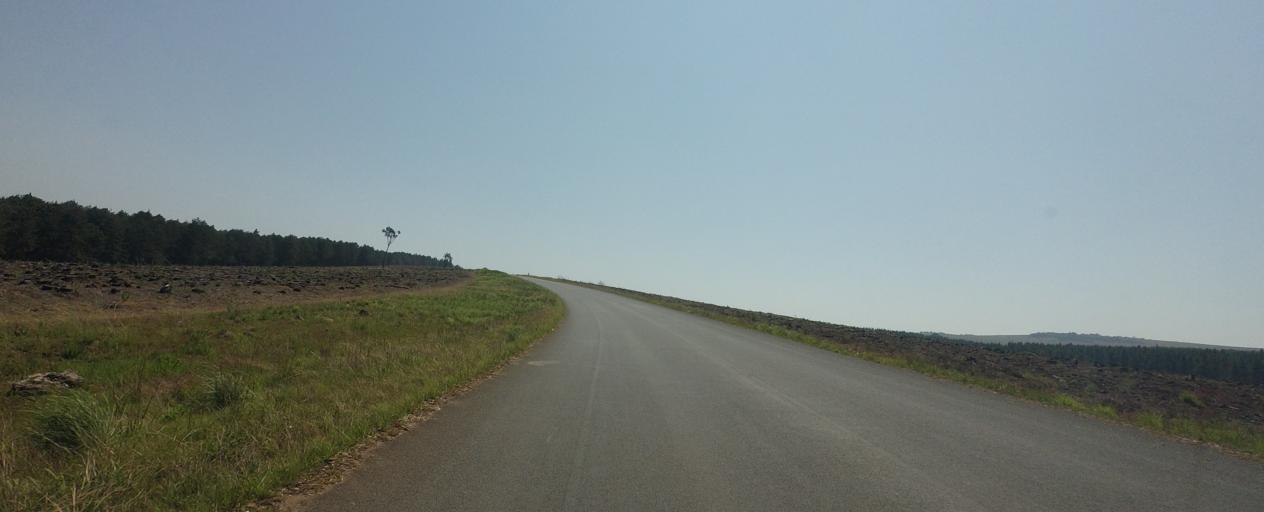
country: ZA
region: Mpumalanga
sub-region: Ehlanzeni District
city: Graksop
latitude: -25.0229
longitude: 30.8227
